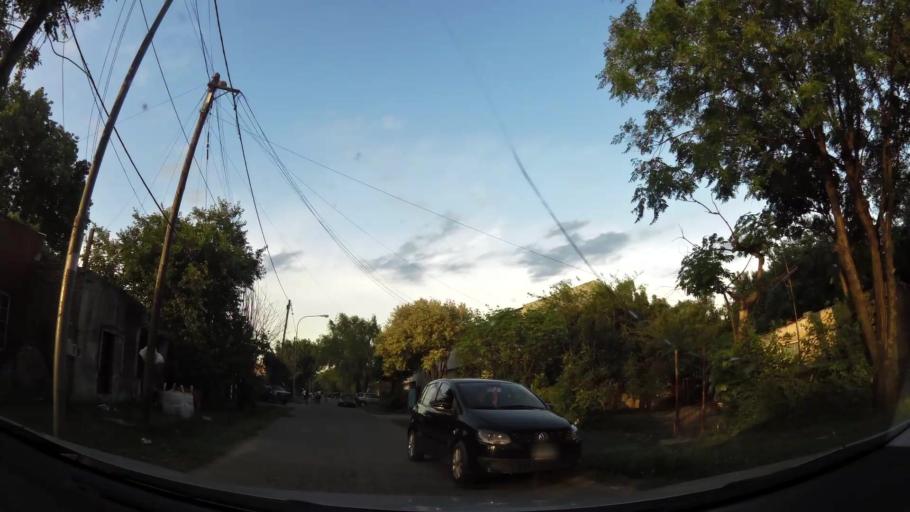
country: AR
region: Buenos Aires
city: Santa Catalina - Dique Lujan
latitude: -34.4465
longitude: -58.6616
